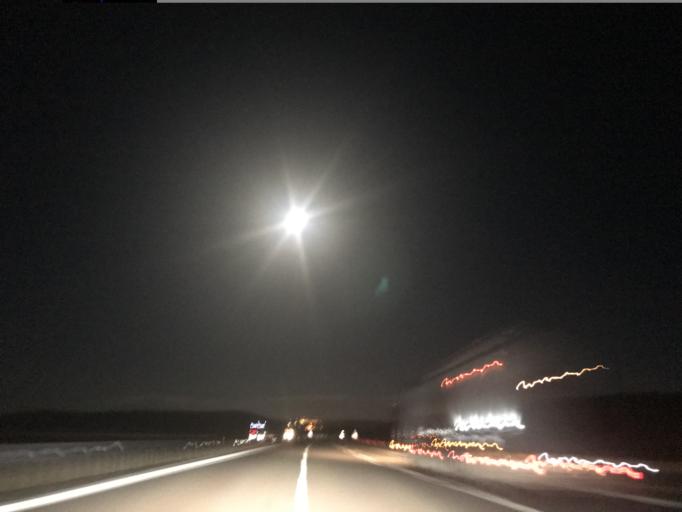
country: TR
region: Nigde
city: Ulukisla
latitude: 37.6357
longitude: 34.4364
